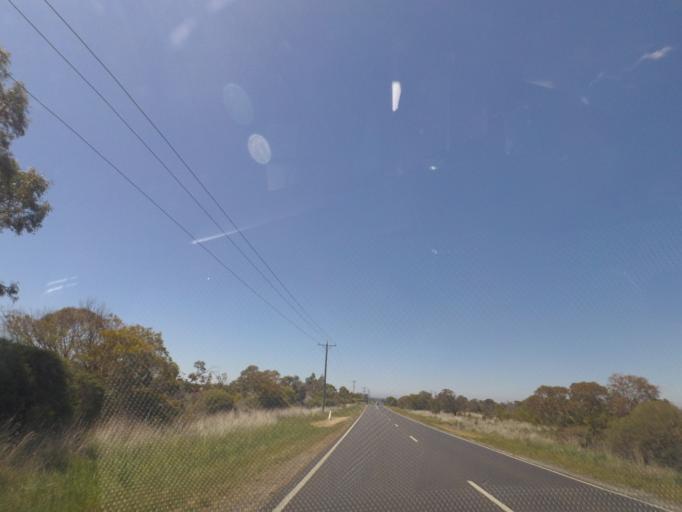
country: AU
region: Victoria
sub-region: Hume
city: Sunbury
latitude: -37.4676
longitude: 144.6561
